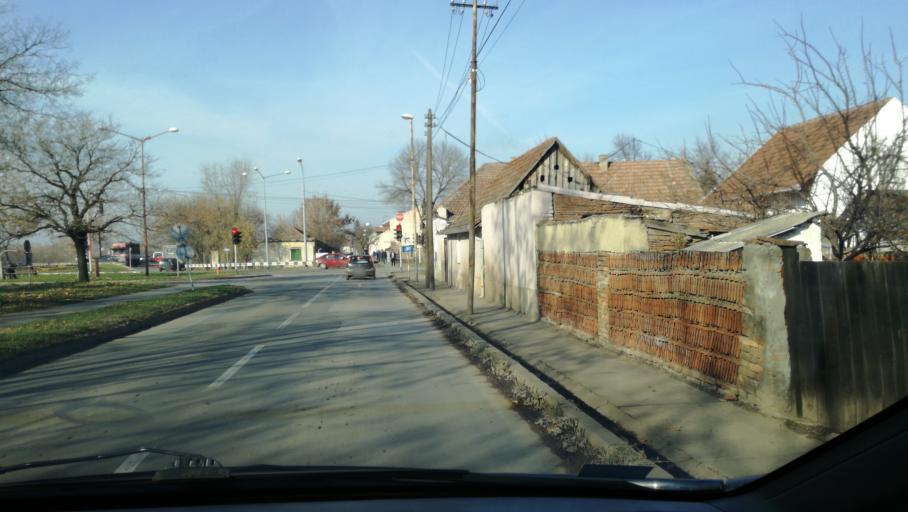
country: RS
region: Autonomna Pokrajina Vojvodina
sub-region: Severnobanatski Okrug
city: Kikinda
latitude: 45.8191
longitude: 20.4491
